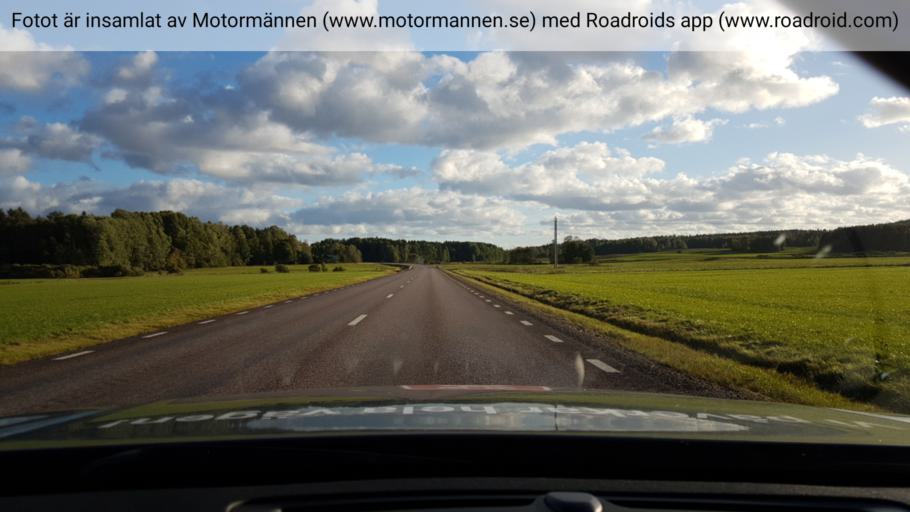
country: SE
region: Vaermland
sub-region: Karlstads Kommun
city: Molkom
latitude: 59.6216
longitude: 13.7302
